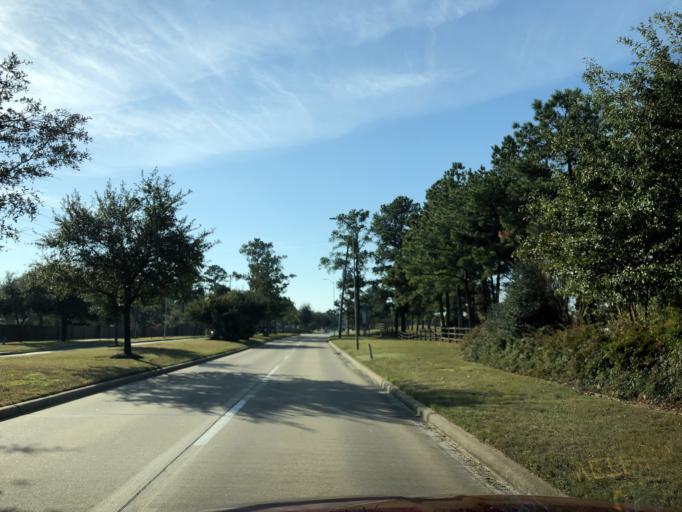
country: US
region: Texas
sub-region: Harris County
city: Tomball
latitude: 30.0451
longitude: -95.5631
